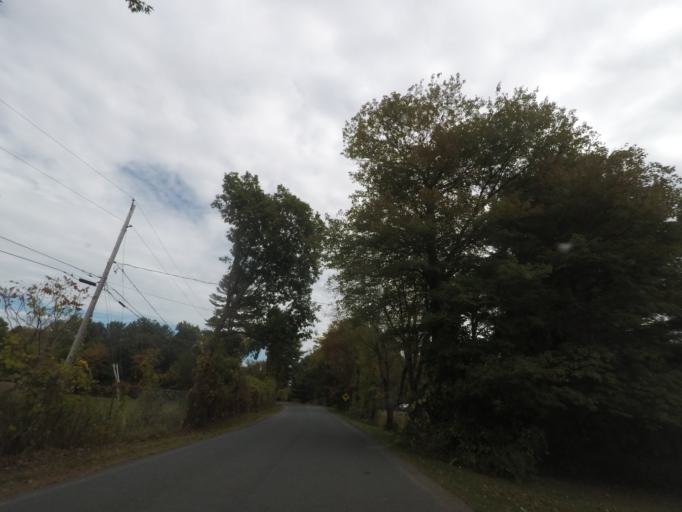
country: US
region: New York
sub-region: Rensselaer County
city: Nassau
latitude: 42.5535
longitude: -73.6528
